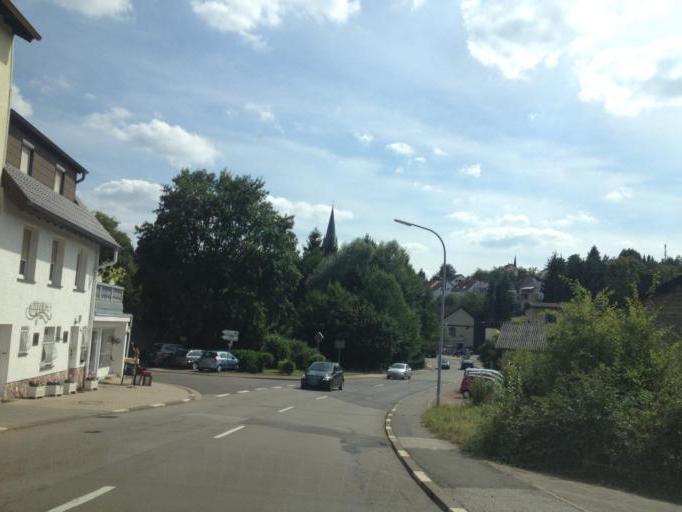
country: DE
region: Saarland
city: Schiffweiler
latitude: 49.3619
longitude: 7.1307
